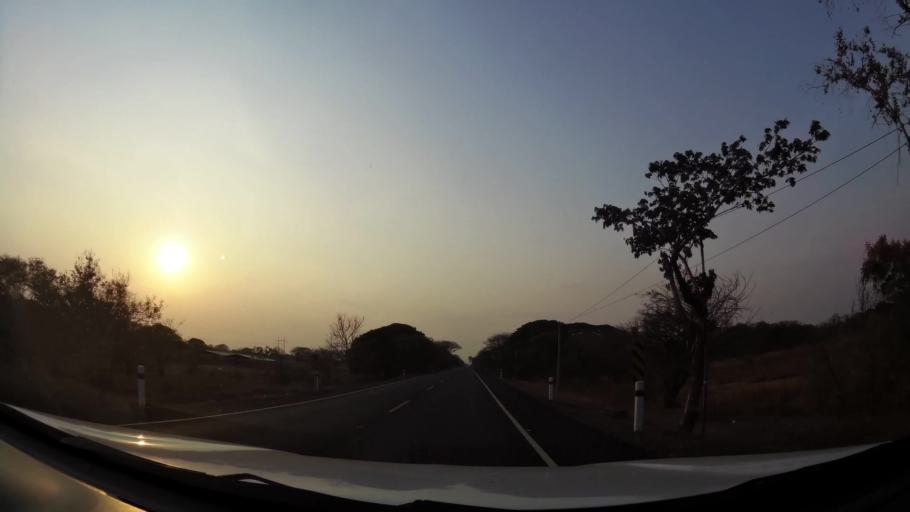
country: NI
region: Leon
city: Nagarote
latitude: 12.2973
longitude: -86.5934
